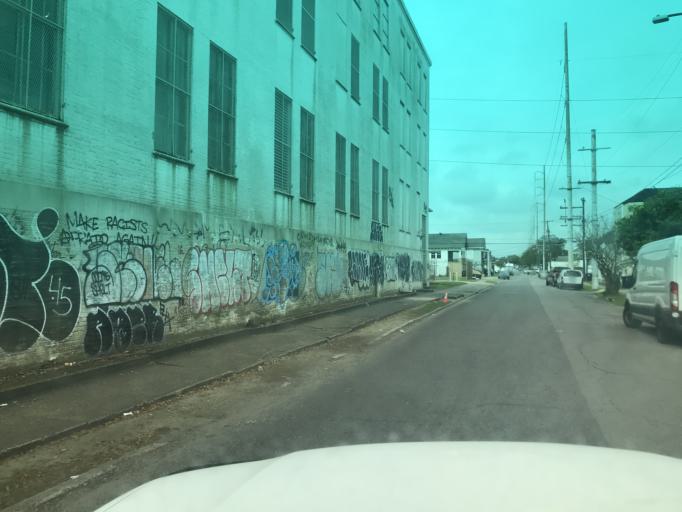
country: US
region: Louisiana
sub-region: Orleans Parish
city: New Orleans
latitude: 29.9762
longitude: -90.0484
